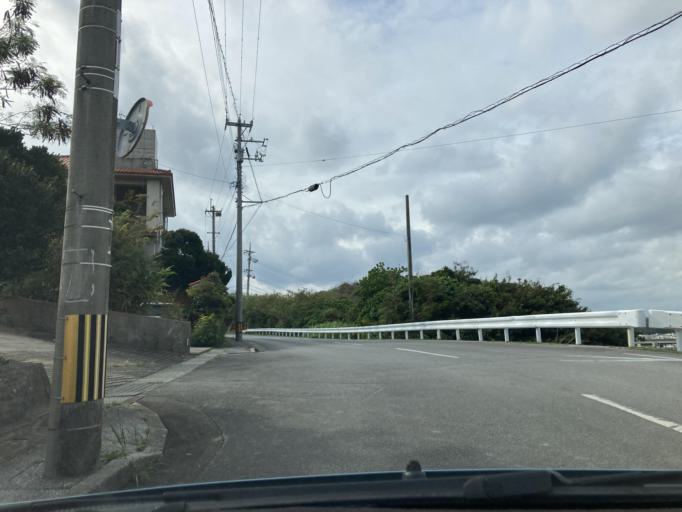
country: JP
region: Okinawa
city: Ginowan
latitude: 26.2089
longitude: 127.7450
